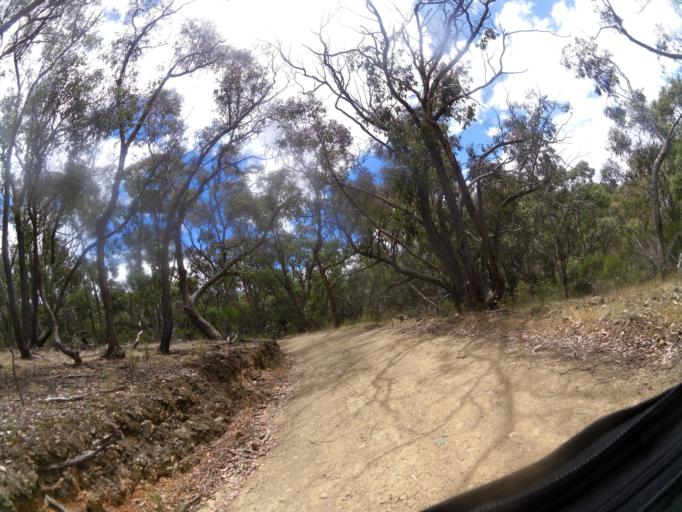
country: AU
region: Victoria
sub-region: Mount Alexander
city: Castlemaine
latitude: -37.0492
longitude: 144.2687
